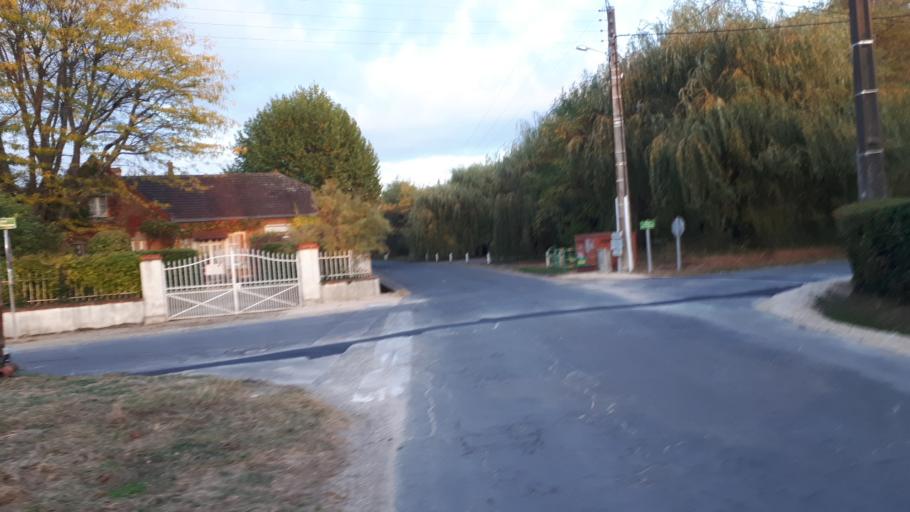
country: FR
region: Centre
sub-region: Departement du Loir-et-Cher
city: Saint-Romain-sur-Cher
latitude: 47.3615
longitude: 1.4073
